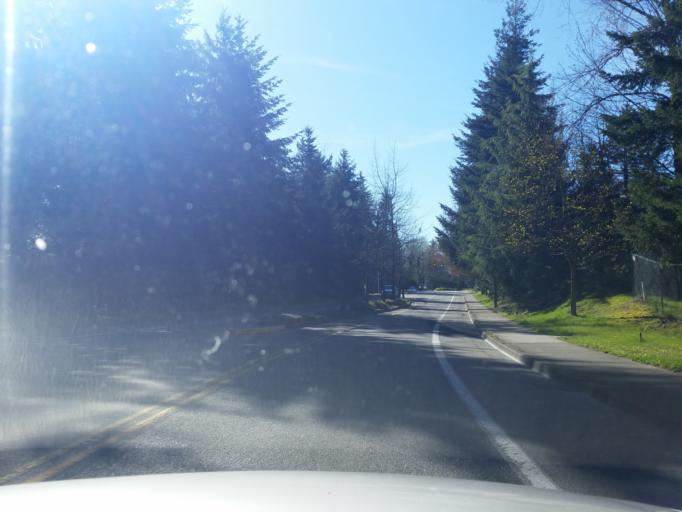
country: US
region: Washington
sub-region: Snohomish County
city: Mill Creek
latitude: 47.8513
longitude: -122.2036
